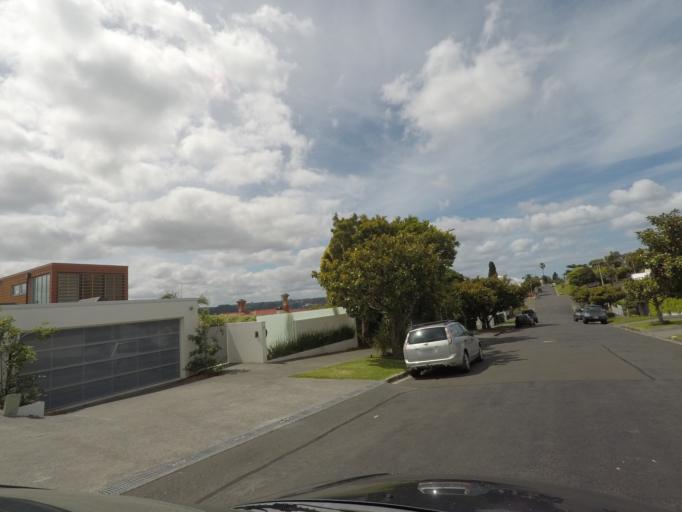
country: NZ
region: Auckland
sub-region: Auckland
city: Auckland
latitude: -36.8467
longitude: 174.7247
